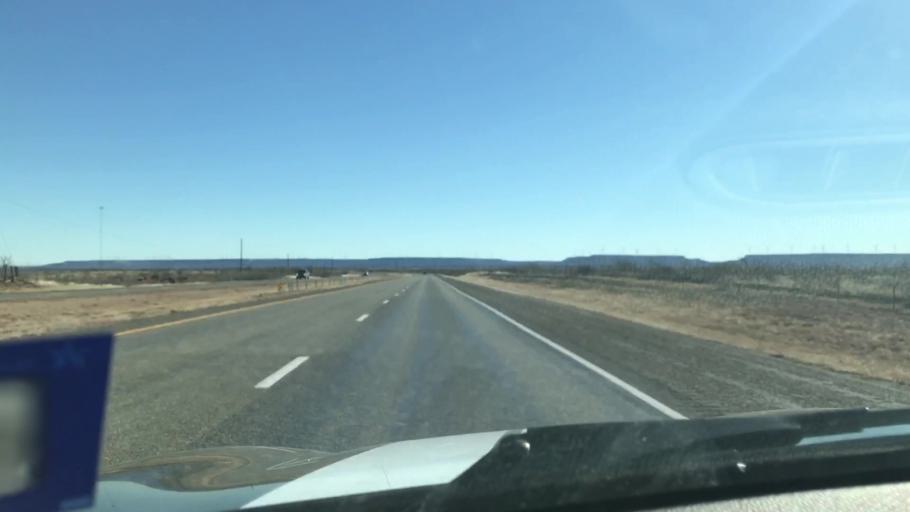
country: US
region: Texas
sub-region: Garza County
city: Post
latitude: 33.0789
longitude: -101.2392
